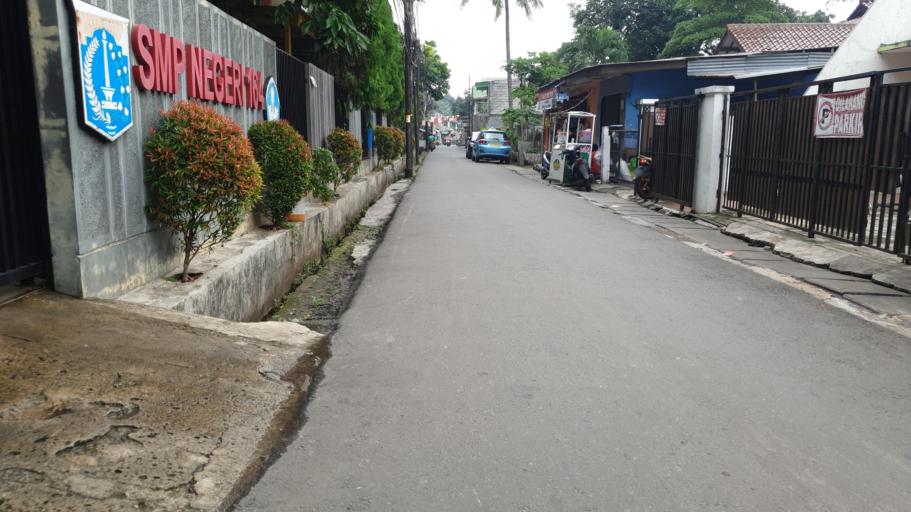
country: ID
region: Banten
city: South Tangerang
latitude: -6.2562
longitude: 106.7831
